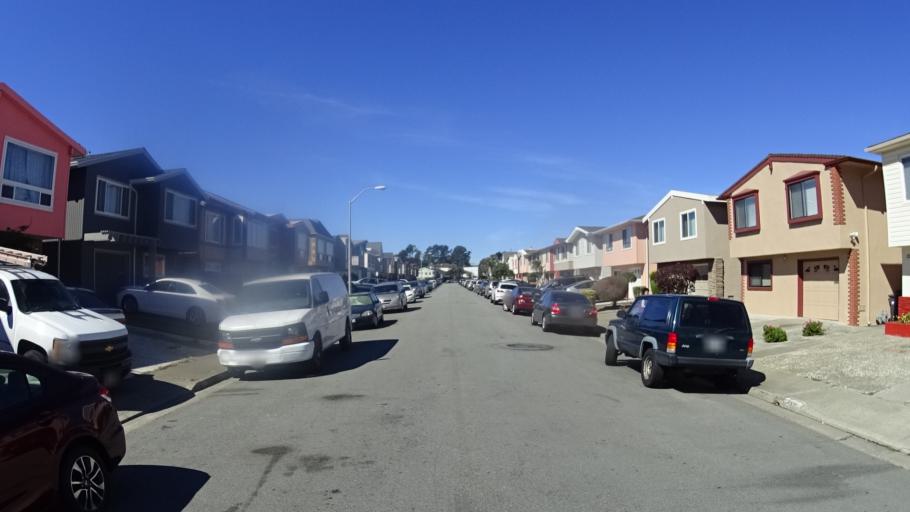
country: US
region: California
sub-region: San Mateo County
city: Broadmoor
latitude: 37.6810
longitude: -122.4759
